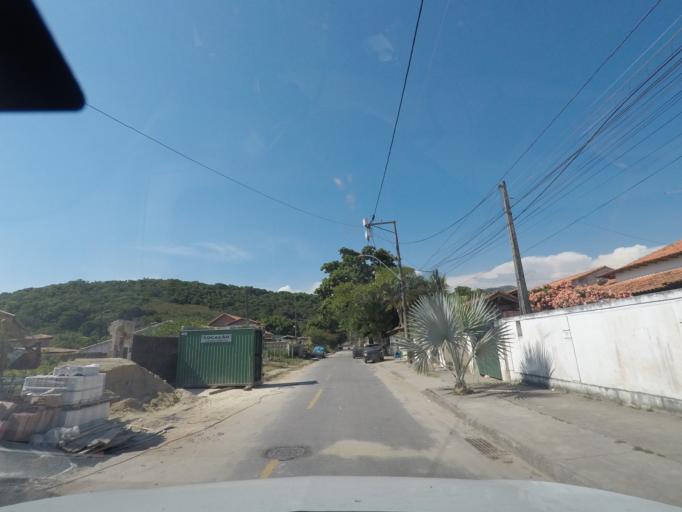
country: BR
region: Rio de Janeiro
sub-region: Niteroi
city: Niteroi
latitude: -22.9606
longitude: -42.9729
